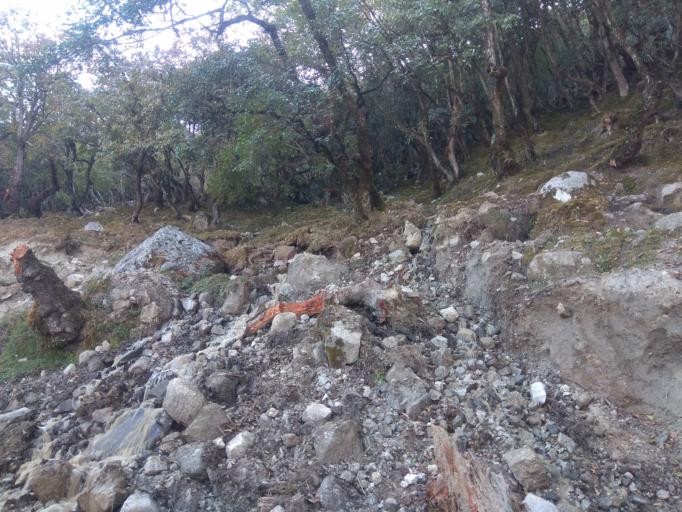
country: NP
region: Far Western
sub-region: Seti Zone
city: Achham
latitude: 29.2706
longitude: 81.6143
